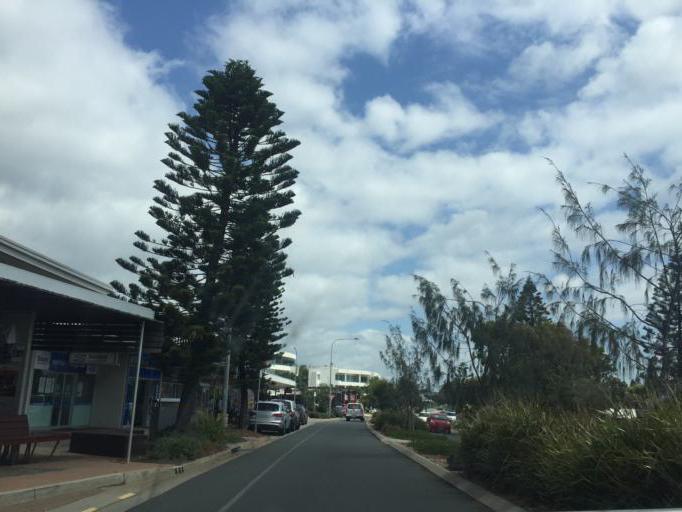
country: AU
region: Queensland
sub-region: Sunshine Coast
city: Coolum Beach
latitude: -26.5300
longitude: 153.0913
